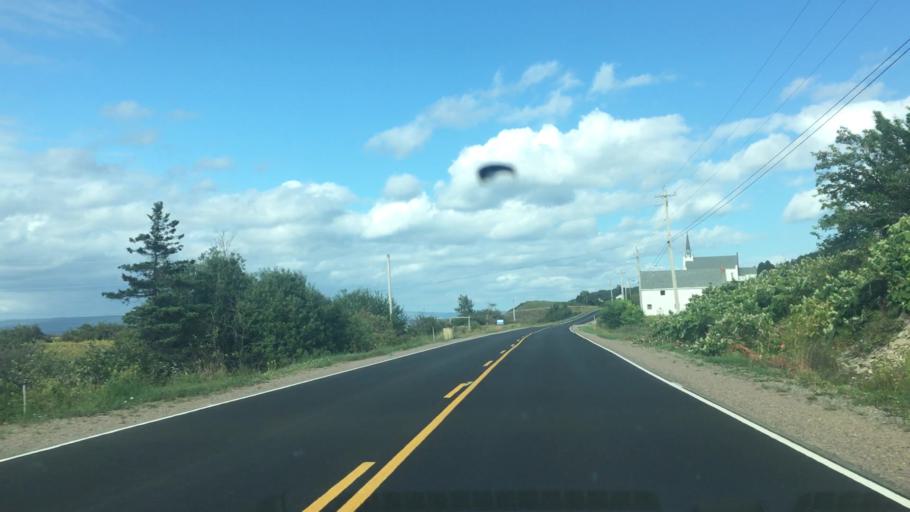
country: CA
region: Nova Scotia
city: Princeville
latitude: 45.7973
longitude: -60.7341
